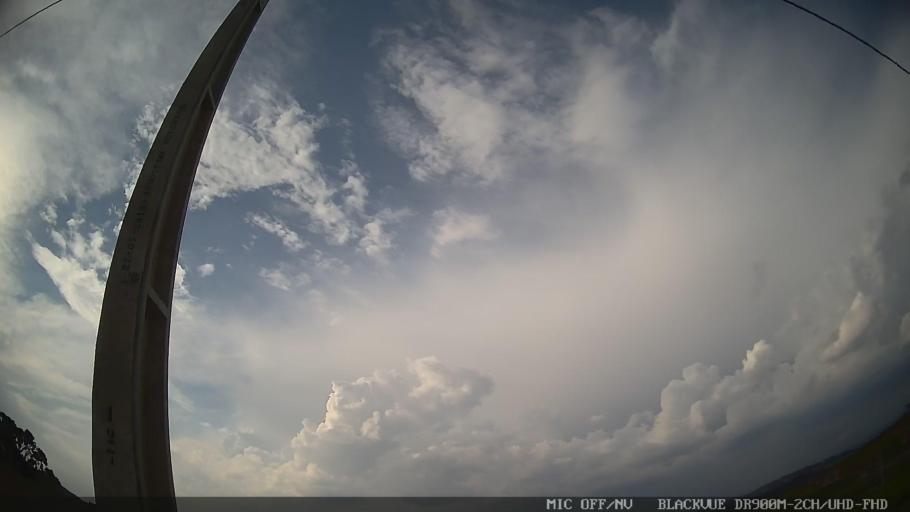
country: BR
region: Sao Paulo
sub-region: Braganca Paulista
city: Braganca Paulista
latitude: -22.9153
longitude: -46.5646
